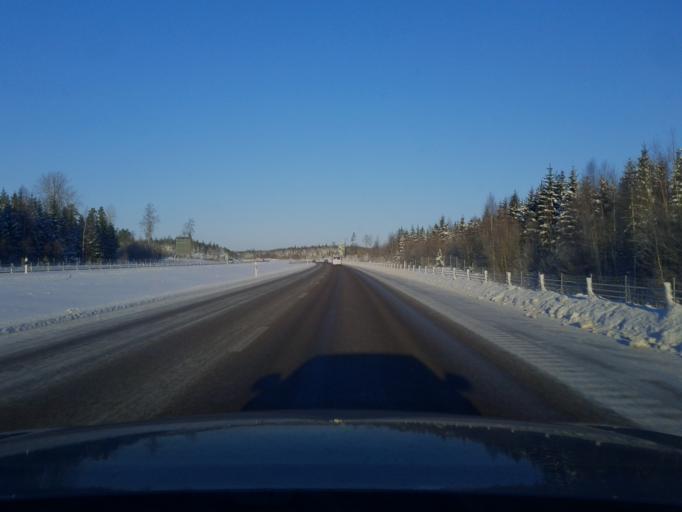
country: SE
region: Uppsala
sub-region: Tierps Kommun
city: Tierp
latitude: 60.3750
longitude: 17.4819
